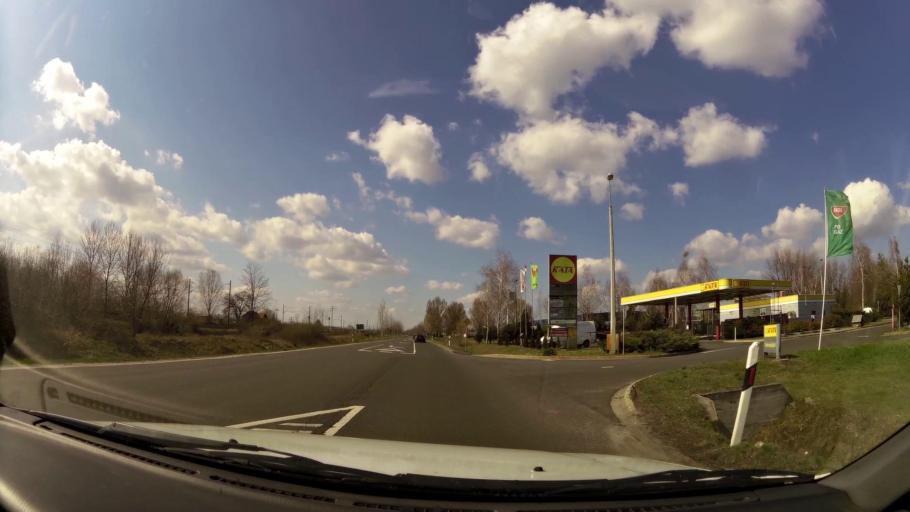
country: HU
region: Pest
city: Nagykata
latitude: 47.3961
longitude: 19.7620
